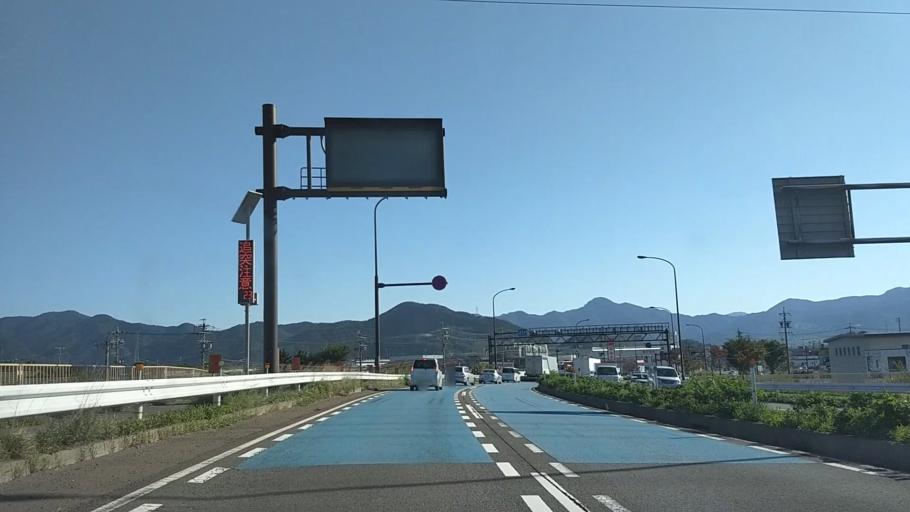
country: JP
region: Nagano
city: Nagano-shi
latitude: 36.5562
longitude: 138.1385
